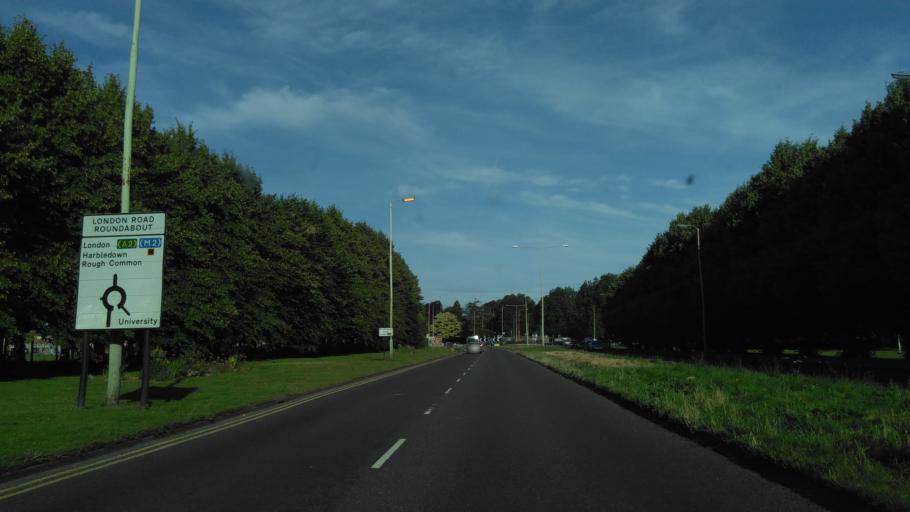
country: GB
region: England
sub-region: Kent
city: Canterbury
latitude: 51.2812
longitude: 1.0661
